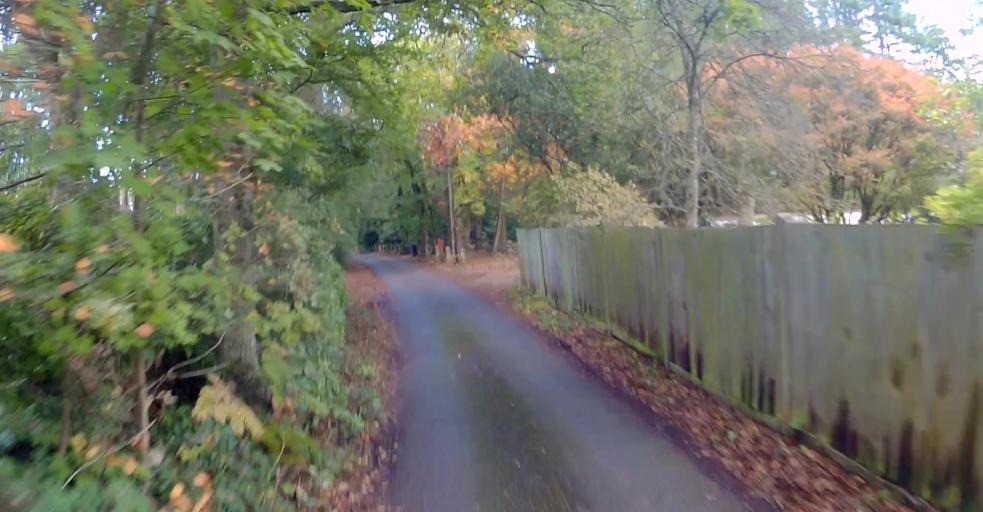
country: GB
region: England
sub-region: Surrey
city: Elstead
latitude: 51.1878
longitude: -0.7372
